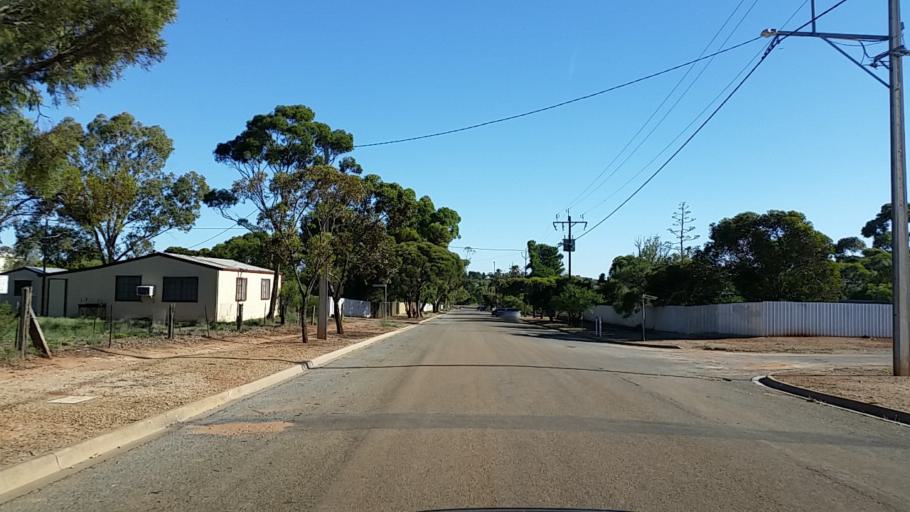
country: AU
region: South Australia
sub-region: Peterborough
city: Peterborough
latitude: -32.9687
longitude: 138.8317
